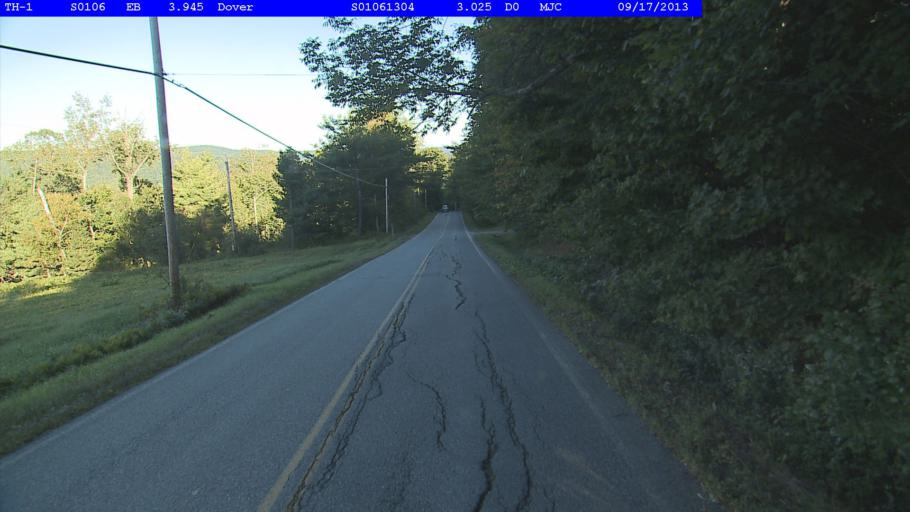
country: US
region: Vermont
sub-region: Windham County
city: Dover
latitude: 42.9460
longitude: -72.7869
